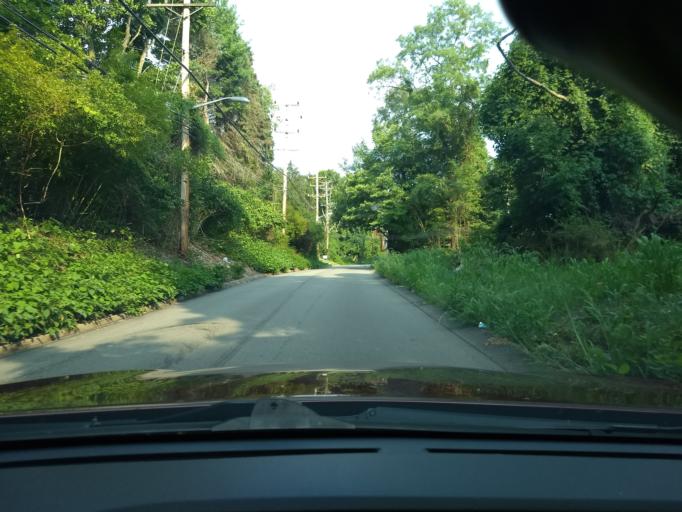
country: US
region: Pennsylvania
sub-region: Allegheny County
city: Aspinwall
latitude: 40.4730
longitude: -79.9004
